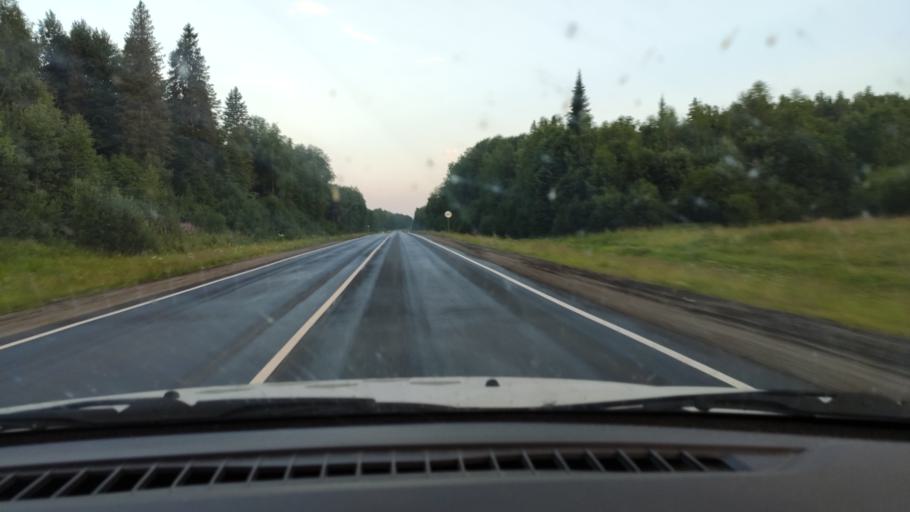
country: RU
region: Perm
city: Zyukayka
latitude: 58.3736
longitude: 54.6393
